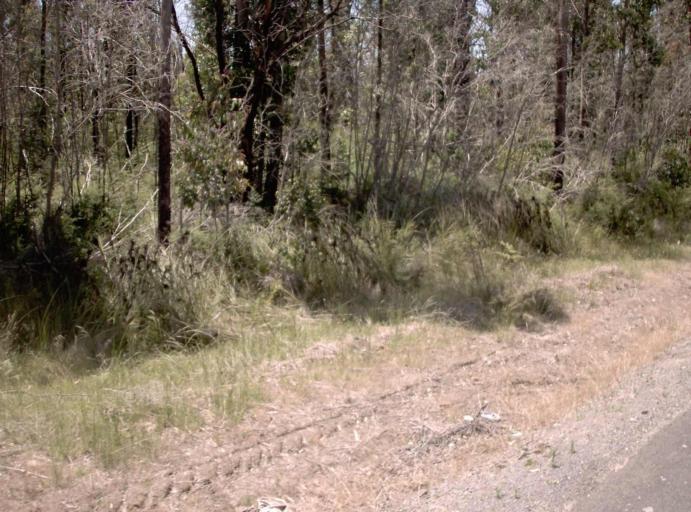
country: AU
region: Victoria
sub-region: East Gippsland
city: Lakes Entrance
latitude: -37.7488
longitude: 148.2283
